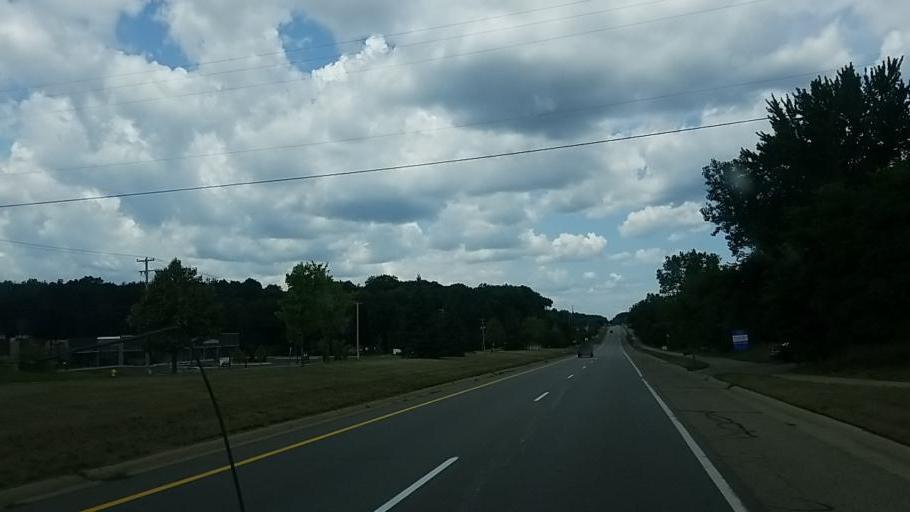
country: US
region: Michigan
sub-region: Kent County
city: Northview
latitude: 43.0035
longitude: -85.5901
